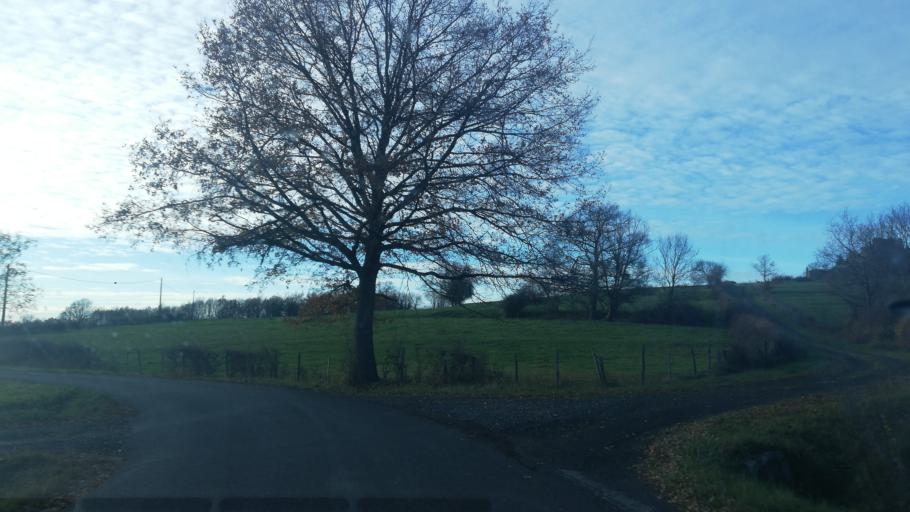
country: FR
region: Auvergne
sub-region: Departement du Puy-de-Dome
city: Billom
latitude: 45.6901
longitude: 3.3654
